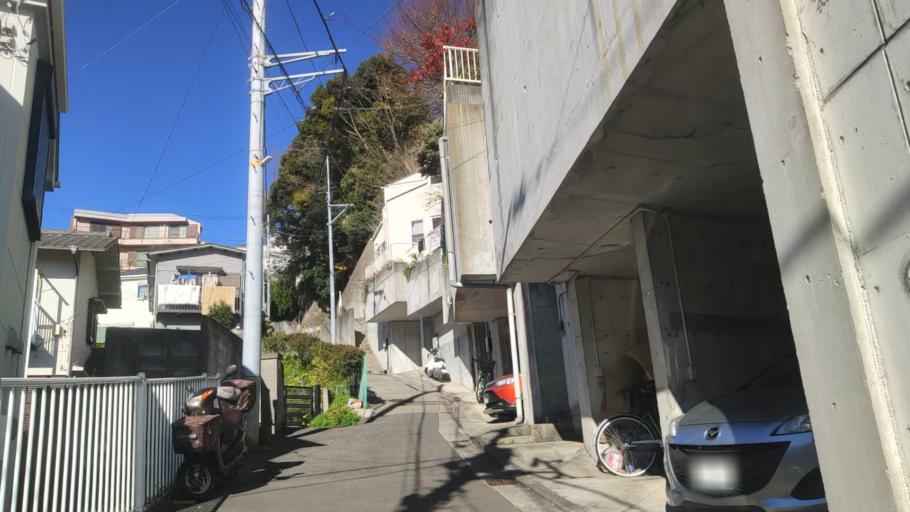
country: JP
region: Kanagawa
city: Yokohama
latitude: 35.4275
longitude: 139.6549
